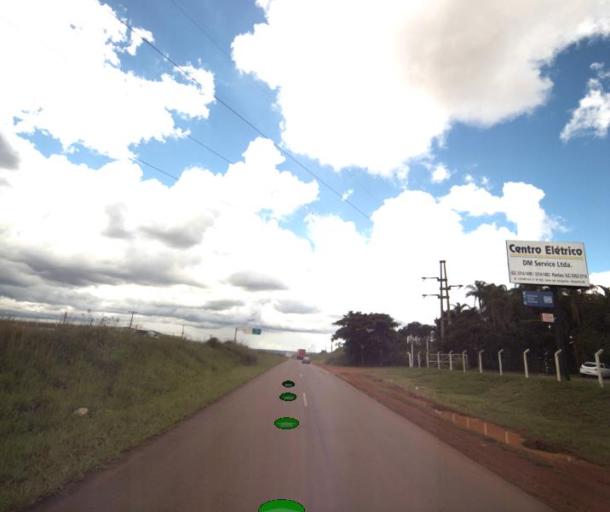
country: BR
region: Goias
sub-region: Anapolis
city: Anapolis
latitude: -16.3593
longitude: -48.9319
